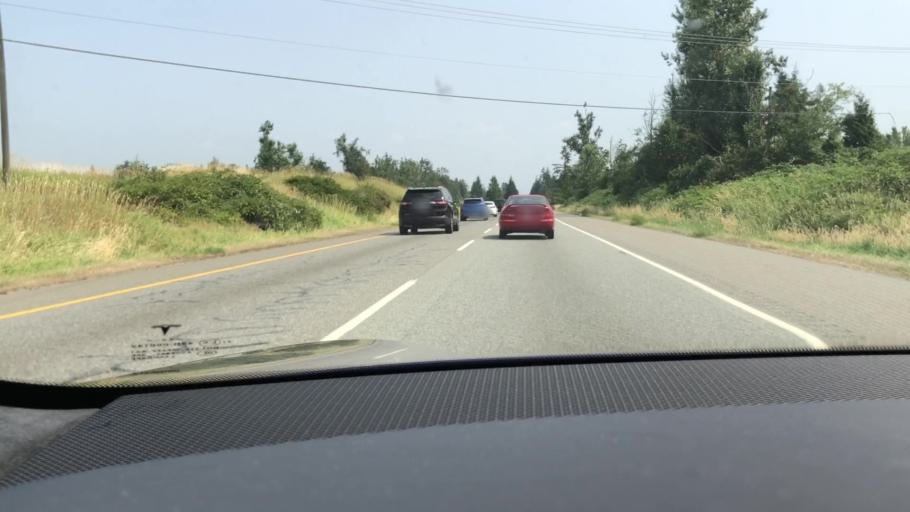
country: CA
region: British Columbia
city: Aldergrove
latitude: 49.0842
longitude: -122.4492
